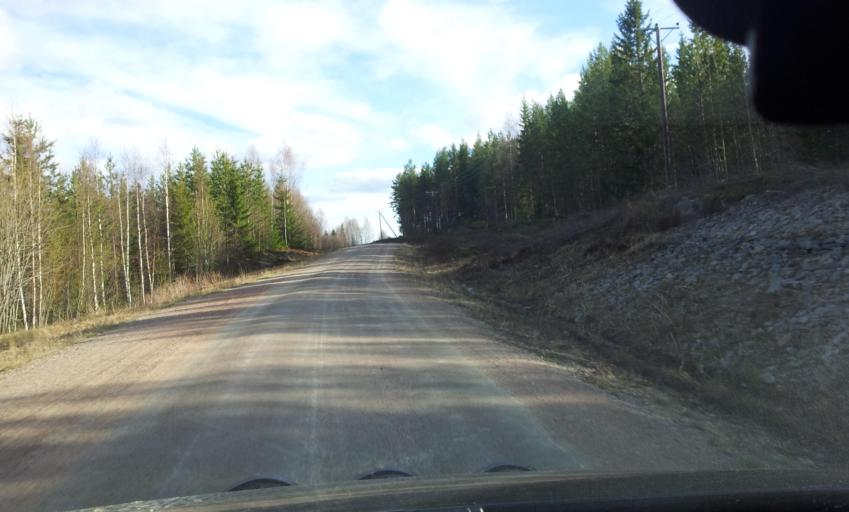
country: SE
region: Vaesternorrland
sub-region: Ange Kommun
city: Ange
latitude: 62.1578
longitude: 15.6622
